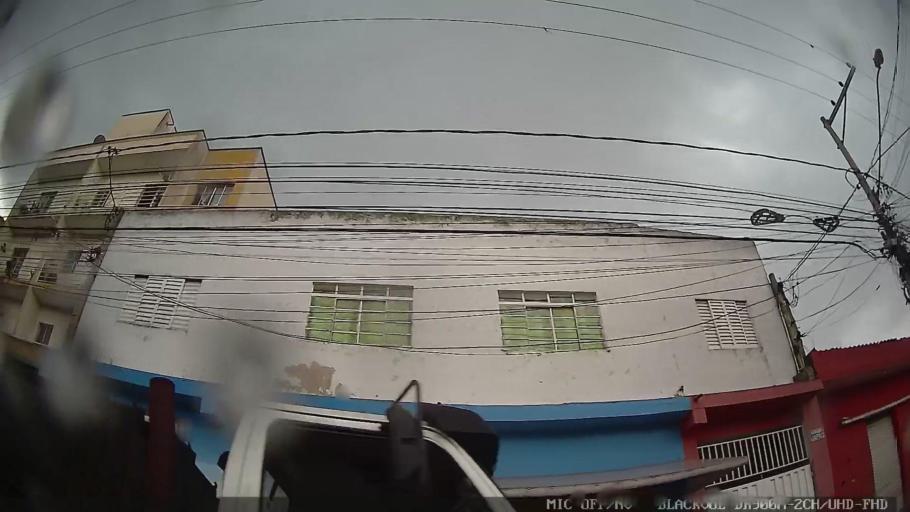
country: BR
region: Sao Paulo
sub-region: Itatiba
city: Itatiba
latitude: -23.0070
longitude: -46.8684
